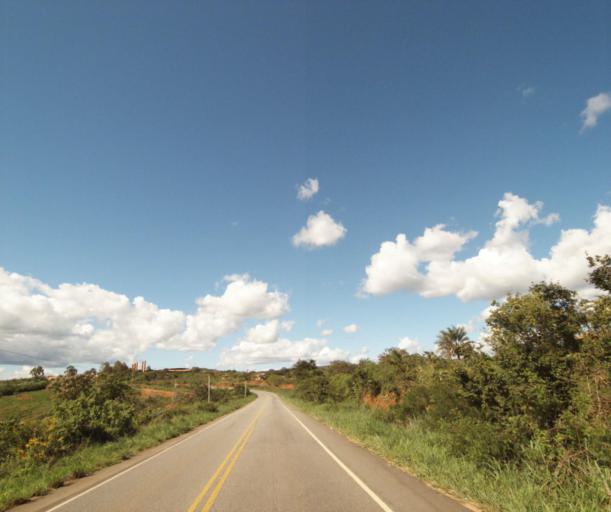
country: BR
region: Bahia
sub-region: Caetite
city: Caetite
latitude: -14.0923
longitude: -42.4477
